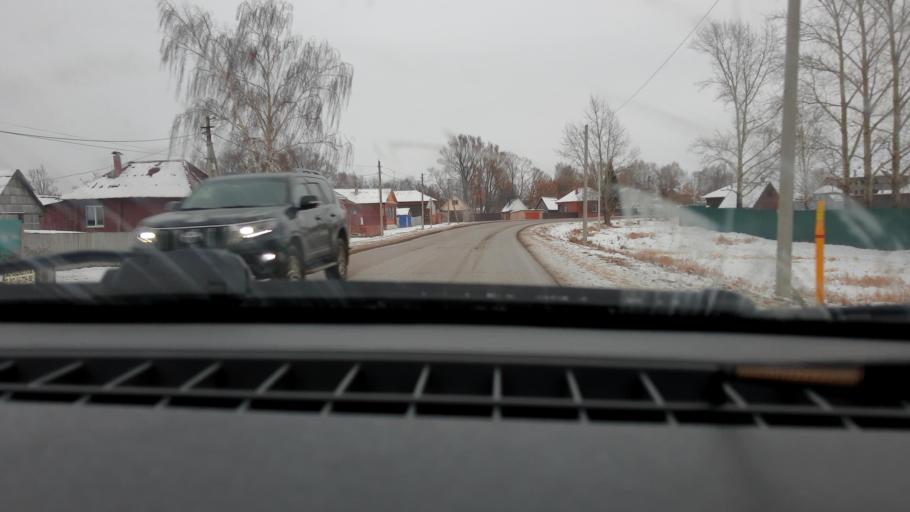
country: RU
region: Bashkortostan
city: Kabakovo
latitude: 54.7053
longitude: 56.2454
